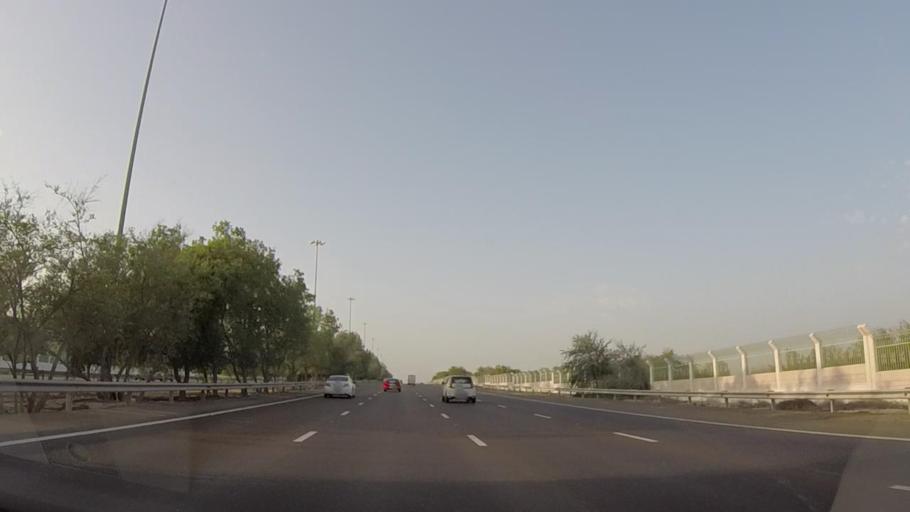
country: AE
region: Dubai
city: Dubai
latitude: 24.8372
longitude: 54.8874
